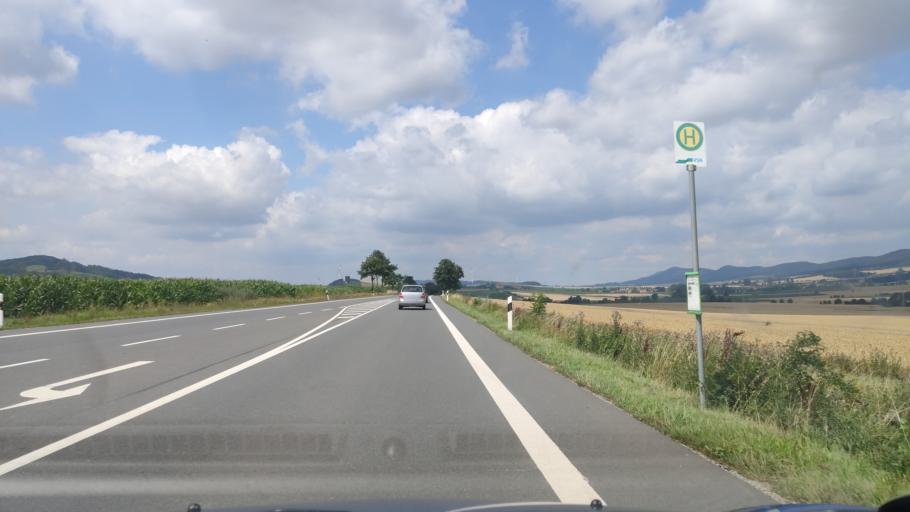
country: DE
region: Lower Saxony
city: Kirchbrak
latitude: 51.9801
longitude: 9.5782
